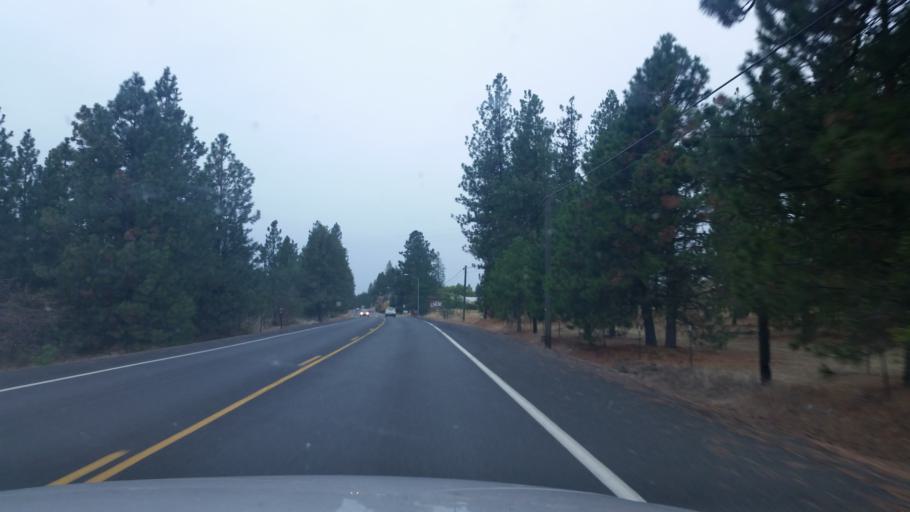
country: US
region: Washington
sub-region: Spokane County
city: Cheney
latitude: 47.5042
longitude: -117.5551
